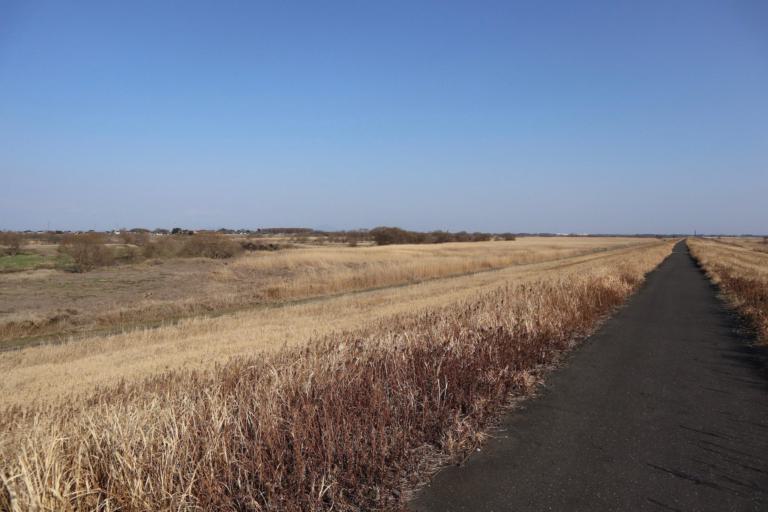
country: JP
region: Tochigi
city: Fujioka
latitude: 36.2621
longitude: 139.6542
